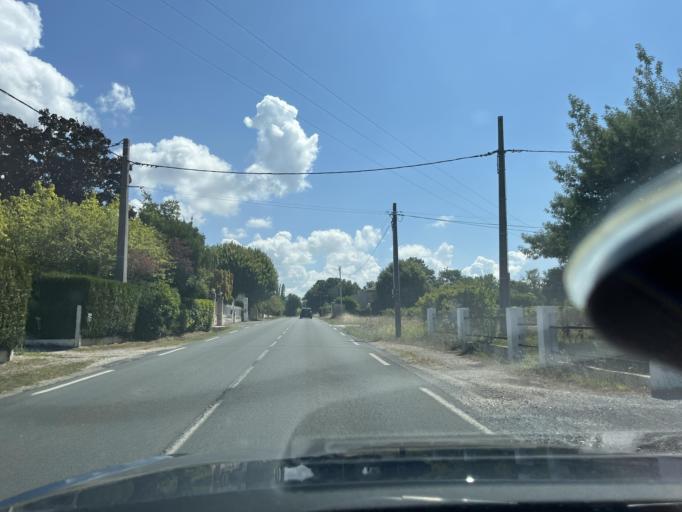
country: FR
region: Aquitaine
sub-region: Departement de la Gironde
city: Cantenac
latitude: 45.0722
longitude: -0.6287
